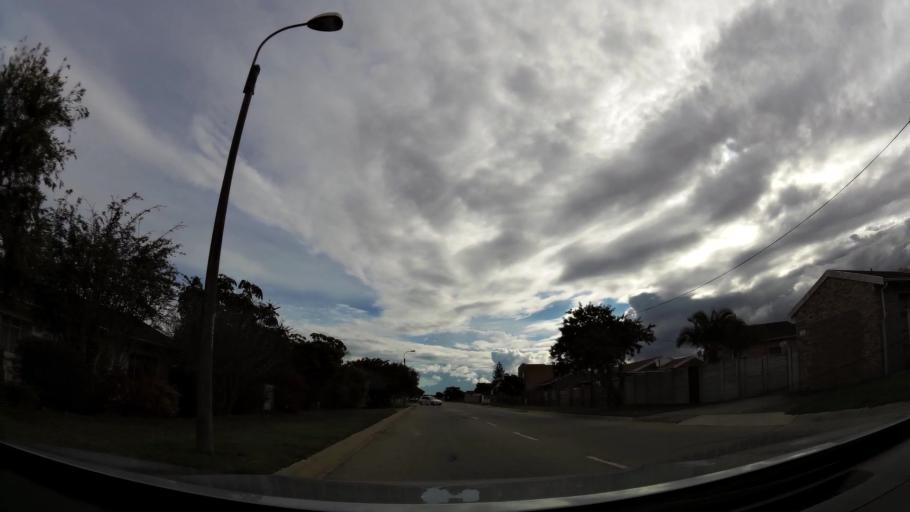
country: ZA
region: Eastern Cape
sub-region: Nelson Mandela Bay Metropolitan Municipality
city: Port Elizabeth
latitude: -33.9423
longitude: 25.4847
